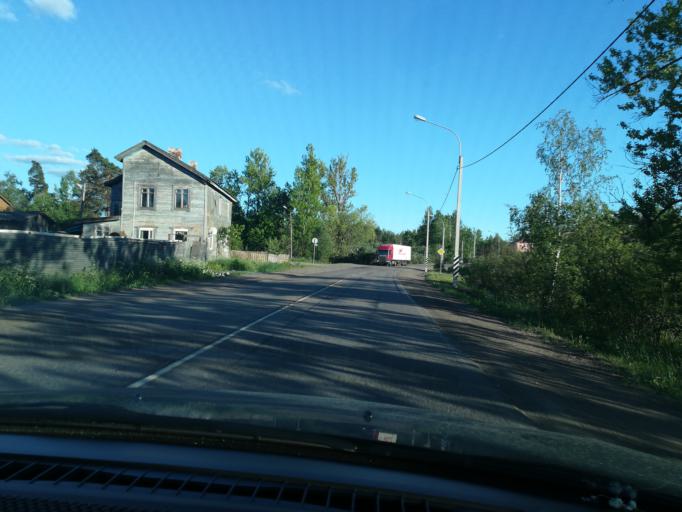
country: RU
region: Leningrad
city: Lesogorskiy
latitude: 61.0473
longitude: 28.9274
